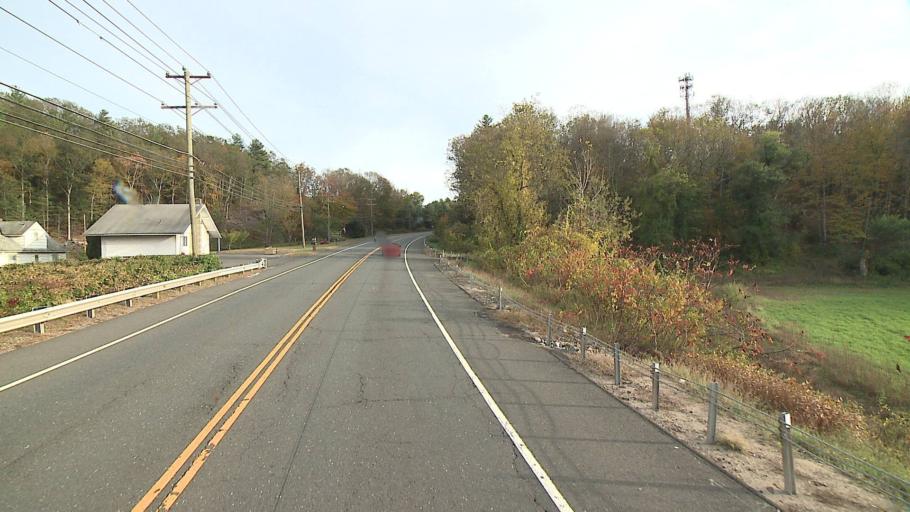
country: US
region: Connecticut
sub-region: Litchfield County
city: New Hartford Center
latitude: 41.8521
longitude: -72.9489
